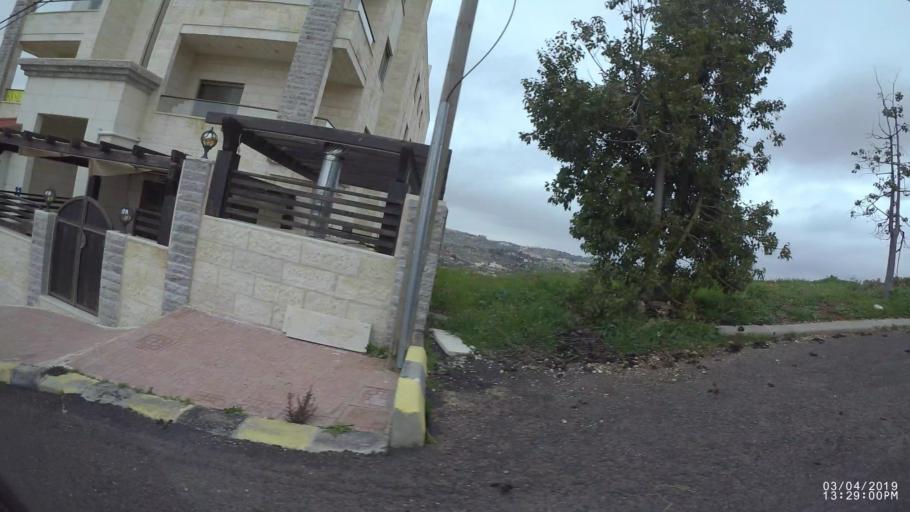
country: JO
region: Amman
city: Wadi as Sir
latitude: 31.9626
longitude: 35.8191
